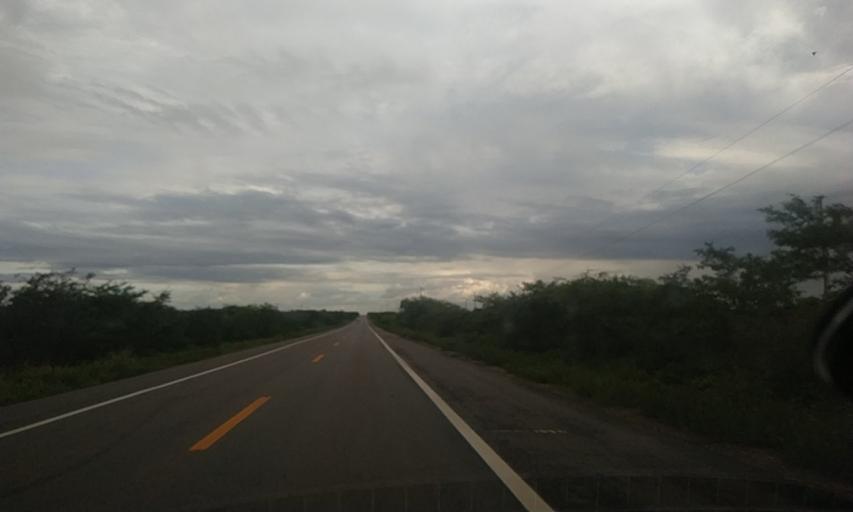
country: BR
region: Rio Grande do Norte
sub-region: Mossoro
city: Mossoro
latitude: -5.1398
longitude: -37.2126
